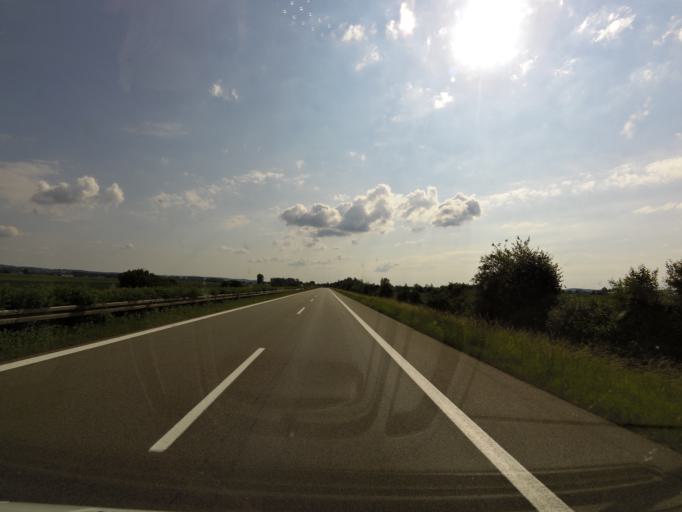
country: DE
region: Bavaria
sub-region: Lower Bavaria
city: Wallersdorf
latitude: 48.7161
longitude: 12.7109
